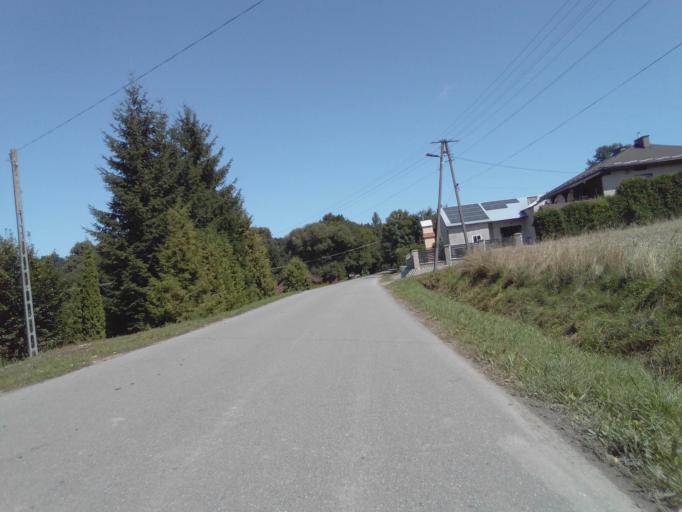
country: PL
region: Subcarpathian Voivodeship
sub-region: Powiat krosnienski
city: Jedlicze
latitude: 49.6702
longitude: 21.6110
